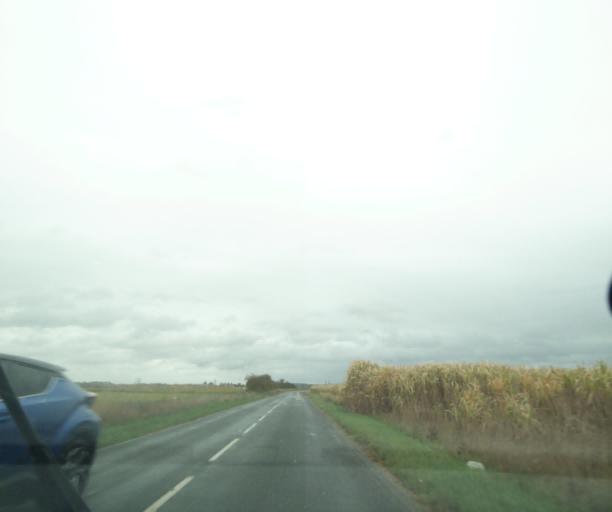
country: FR
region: Rhone-Alpes
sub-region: Departement de l'Ain
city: Loyettes
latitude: 45.7952
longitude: 5.2269
